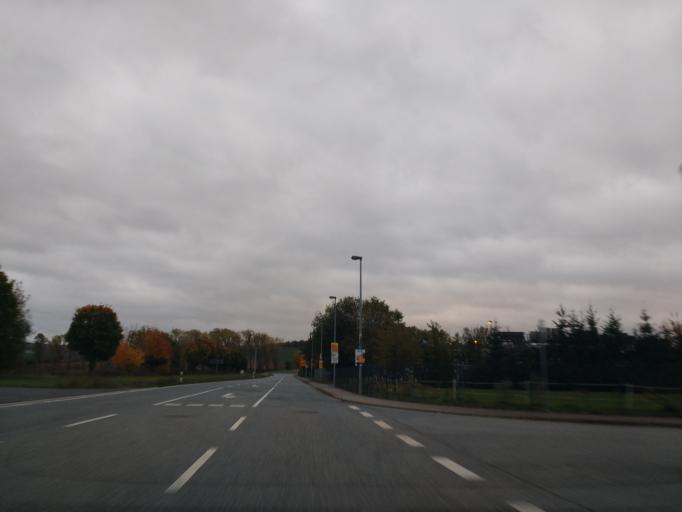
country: DE
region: Thuringia
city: Buhla
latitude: 51.4144
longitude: 10.4382
